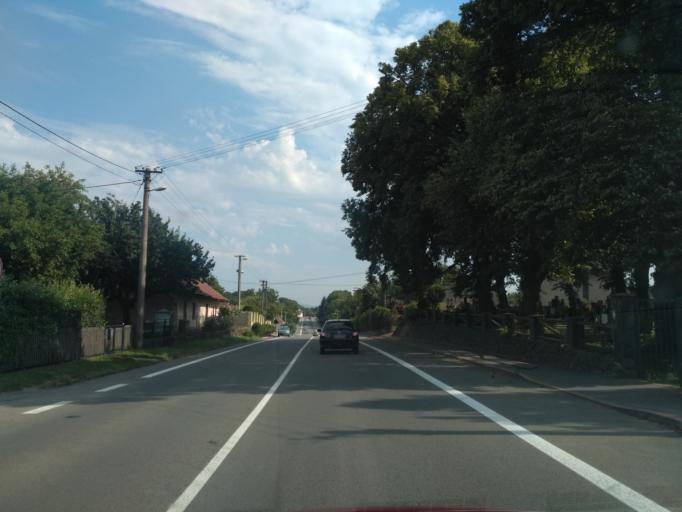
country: SK
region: Kosicky
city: Kosice
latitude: 48.8020
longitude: 21.3028
